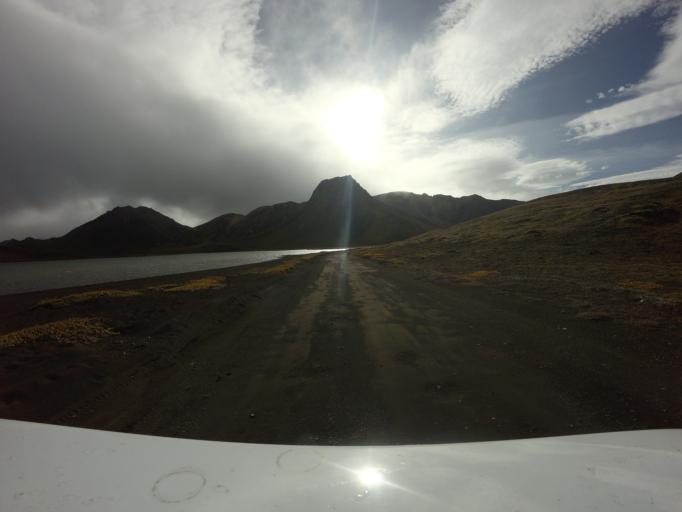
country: IS
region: South
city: Vestmannaeyjar
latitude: 63.9952
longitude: -18.9912
